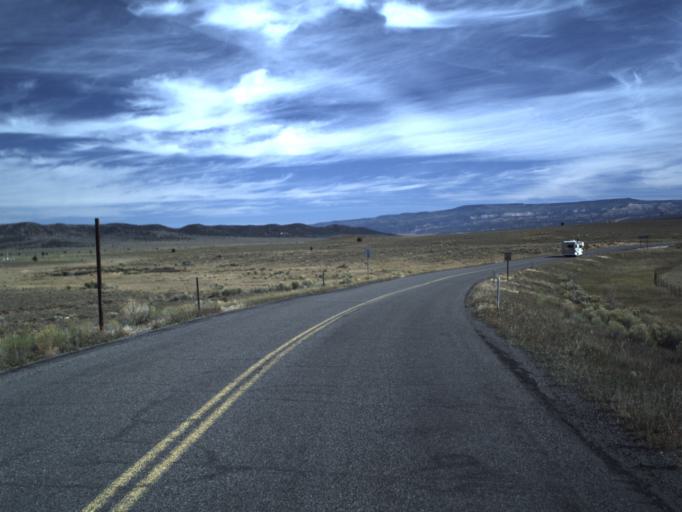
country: US
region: Utah
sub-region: Garfield County
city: Panguitch
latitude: 37.6932
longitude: -112.1516
